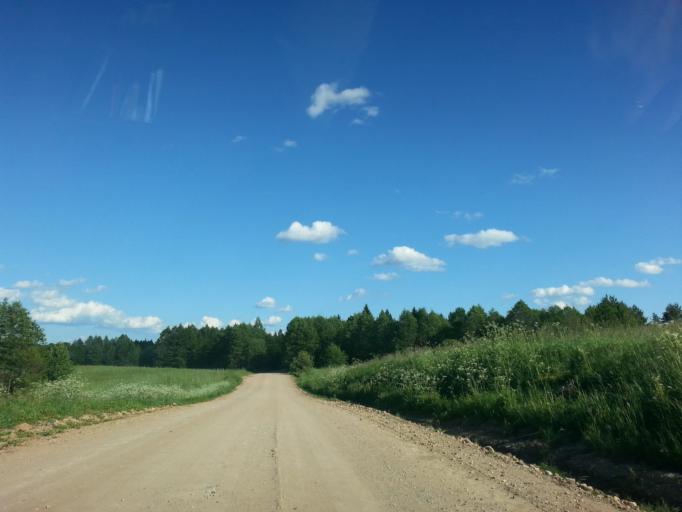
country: BY
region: Minsk
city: Narach
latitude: 54.9764
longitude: 26.6225
